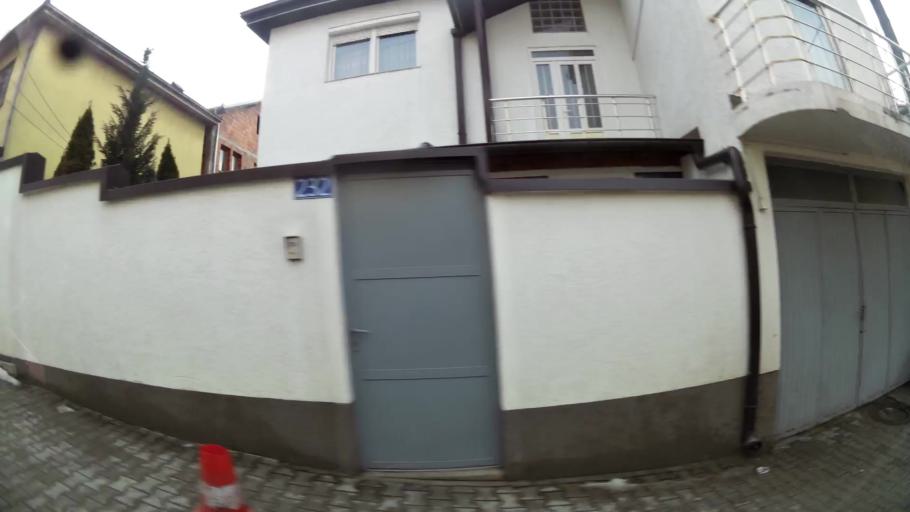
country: XK
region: Pristina
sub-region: Komuna e Prishtines
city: Pristina
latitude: 42.6705
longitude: 21.1698
